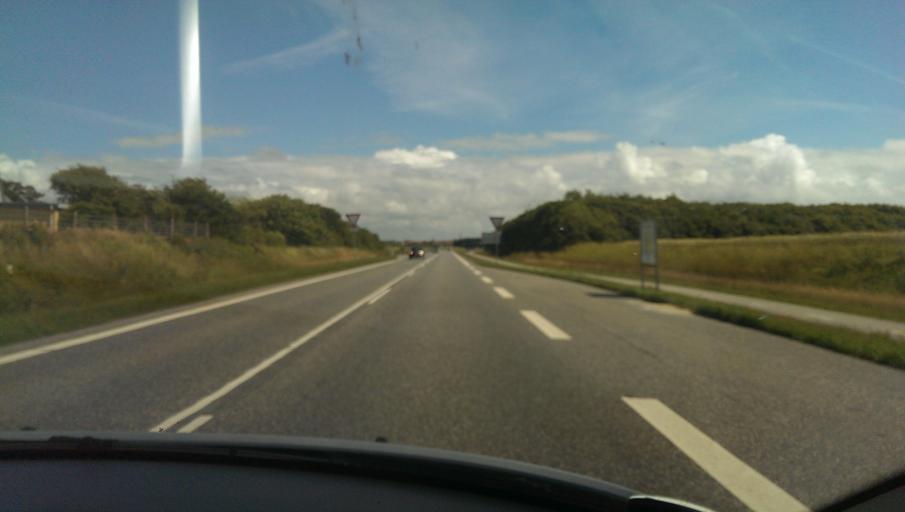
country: DK
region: Central Jutland
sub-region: Ringkobing-Skjern Kommune
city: Ringkobing
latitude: 56.1025
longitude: 8.2174
